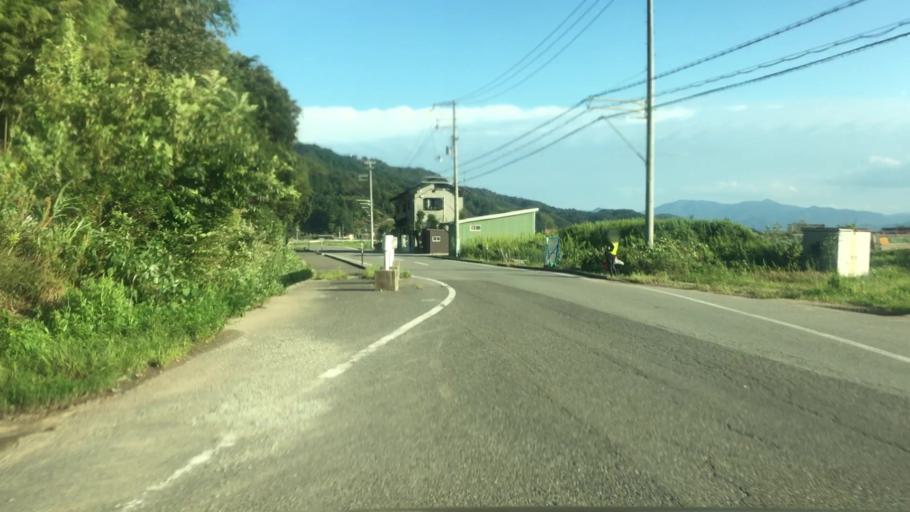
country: JP
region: Hyogo
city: Toyooka
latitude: 35.5867
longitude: 134.8054
